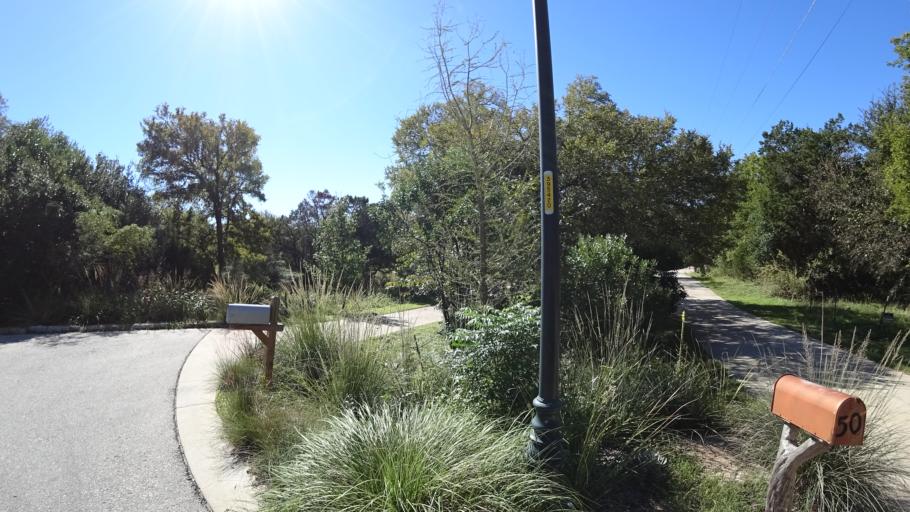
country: US
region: Texas
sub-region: Travis County
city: Rollingwood
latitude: 30.2203
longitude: -97.8125
